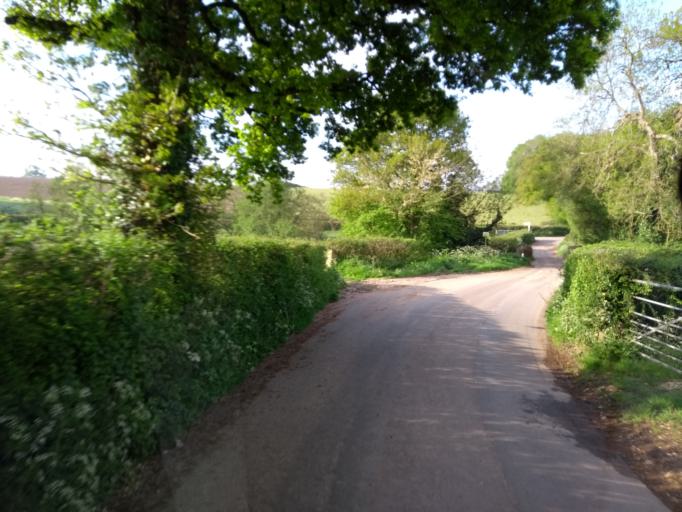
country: GB
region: England
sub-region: Devon
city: Axminster
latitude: 50.8159
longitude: -2.9515
